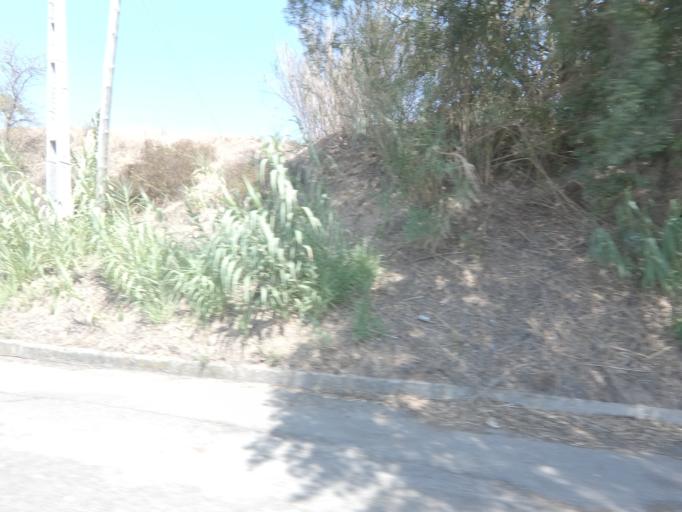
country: PT
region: Setubal
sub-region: Palmela
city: Palmela
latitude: 38.5574
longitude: -8.8867
